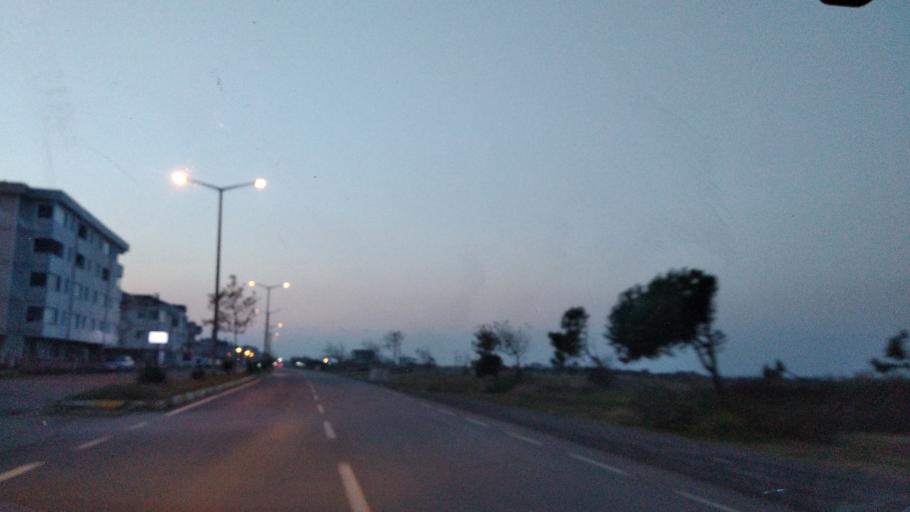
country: TR
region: Sakarya
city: Karasu
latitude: 41.0970
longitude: 30.7283
